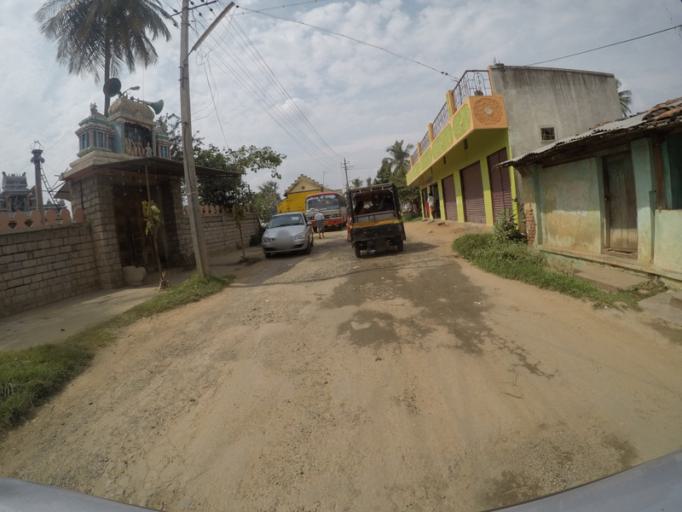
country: IN
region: Karnataka
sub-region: Mandya
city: Malavalli
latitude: 12.4243
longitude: 77.2250
